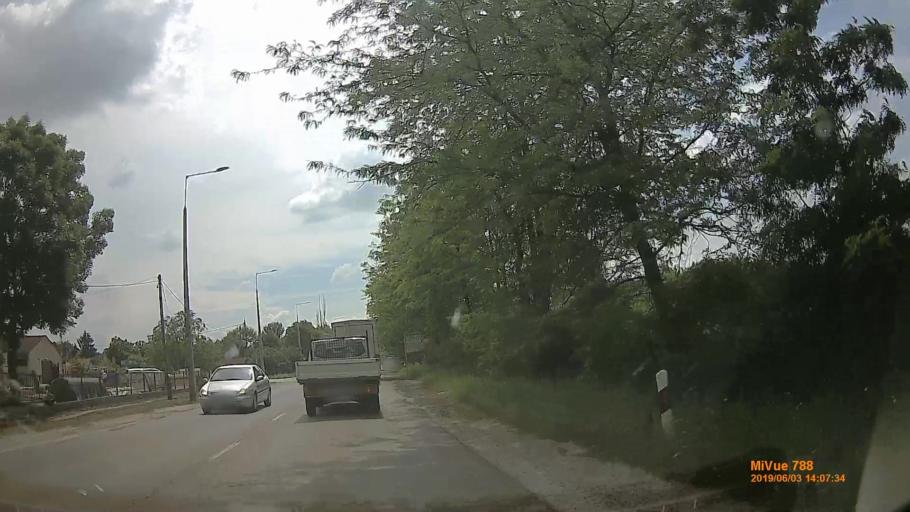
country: HU
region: Jasz-Nagykun-Szolnok
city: Toszeg
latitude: 47.1409
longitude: 20.1572
